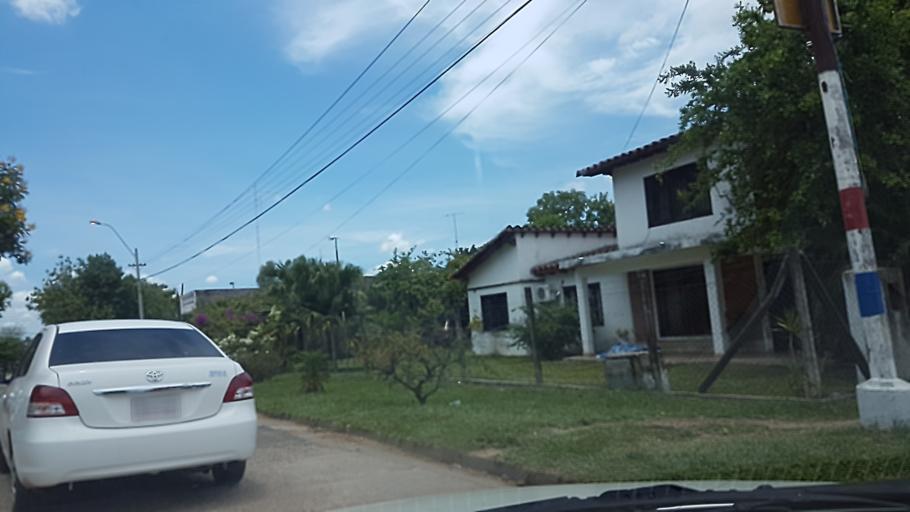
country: PY
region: Central
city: Colonia Mariano Roque Alonso
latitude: -25.2133
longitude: -57.5342
